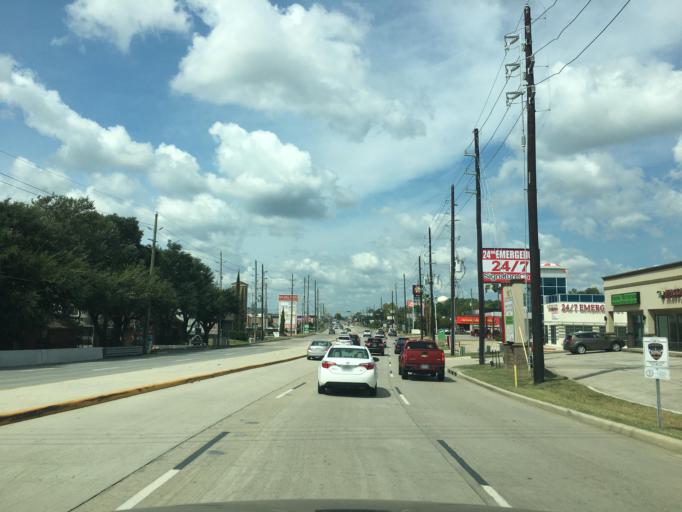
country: US
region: Texas
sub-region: Montgomery County
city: Oak Ridge North
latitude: 30.1275
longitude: -95.4313
